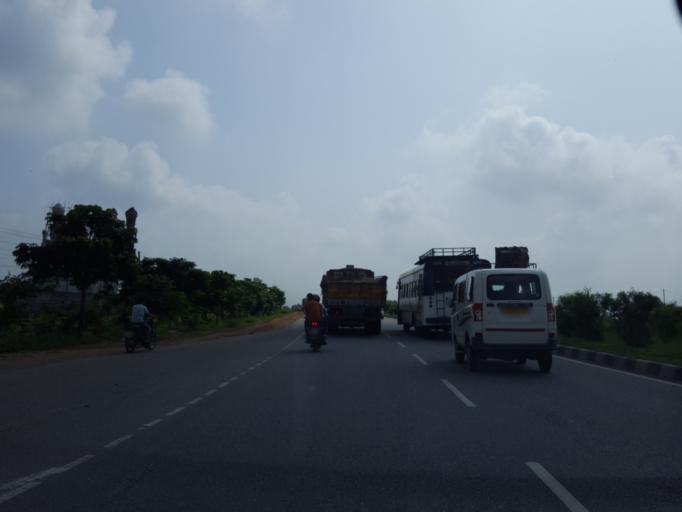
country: IN
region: Telangana
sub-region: Nalgonda
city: Gudur
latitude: 17.2587
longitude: 78.8483
